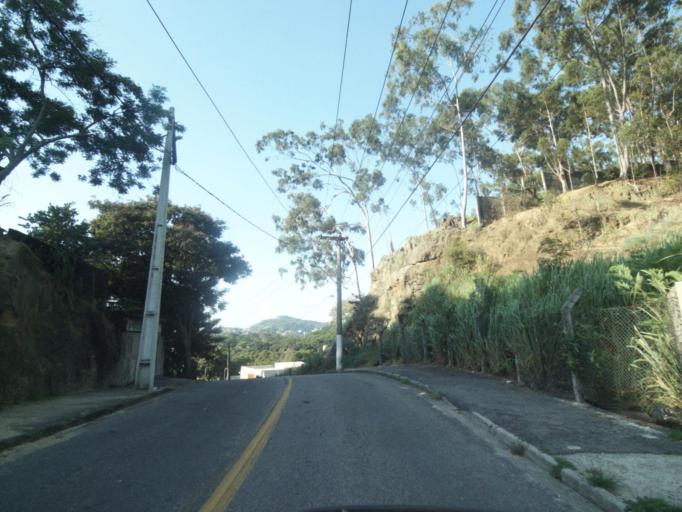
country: BR
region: Rio de Janeiro
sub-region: Niteroi
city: Niteroi
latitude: -22.8882
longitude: -43.0936
